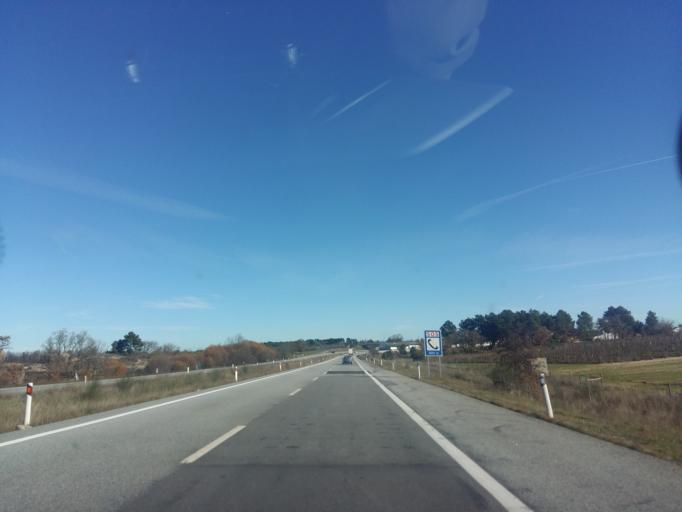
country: PT
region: Guarda
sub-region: Guarda
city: Sequeira
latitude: 40.6015
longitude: -7.1096
